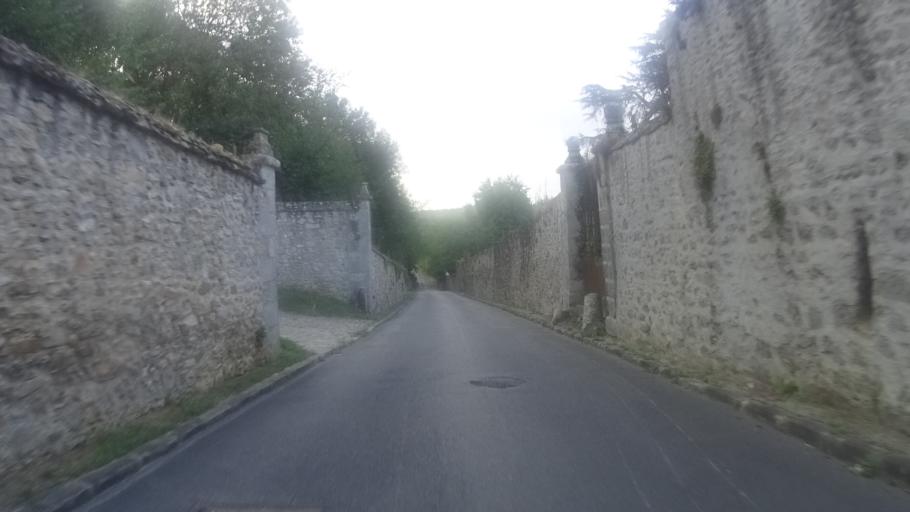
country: FR
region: Ile-de-France
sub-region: Departement de l'Essonne
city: Mennecy
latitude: 48.5709
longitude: 2.4108
